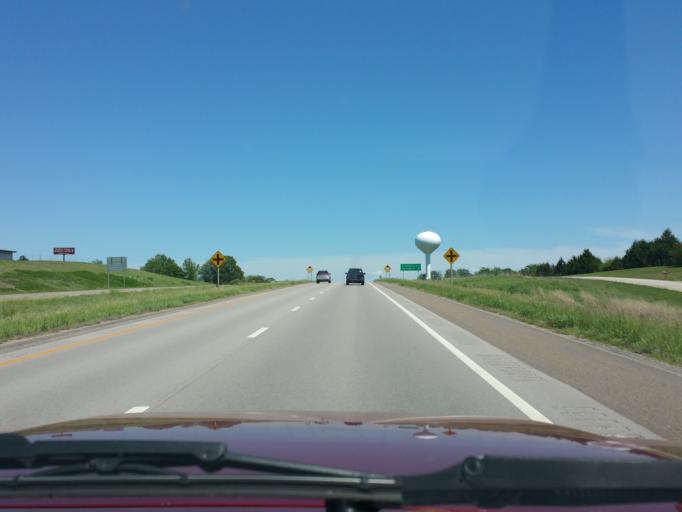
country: US
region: Kansas
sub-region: Pottawatomie County
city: Wamego
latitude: 39.2102
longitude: -96.3350
